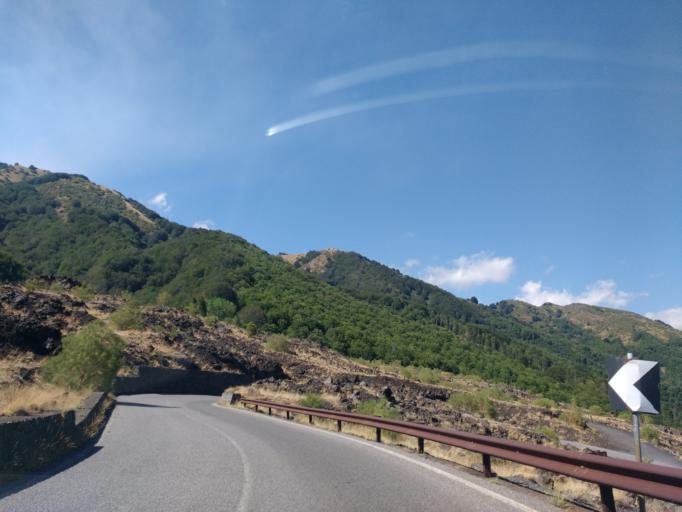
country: IT
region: Sicily
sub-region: Catania
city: Zafferana Etnea
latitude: 37.6969
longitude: 15.0455
